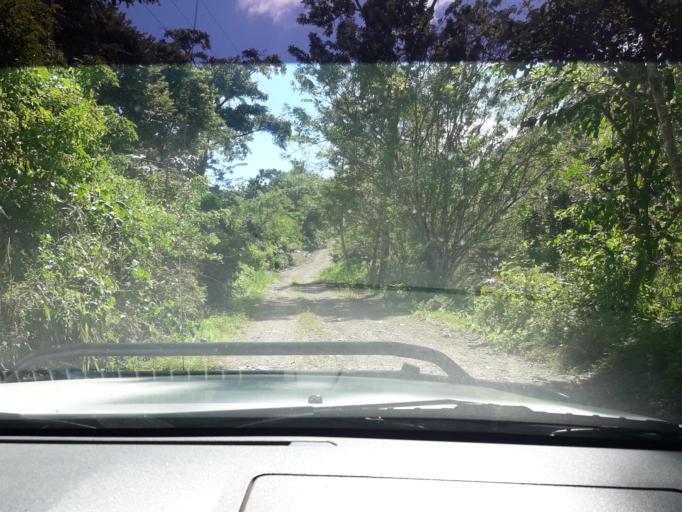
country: CR
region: Guanacaste
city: La Cruz
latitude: 11.1727
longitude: -85.6619
